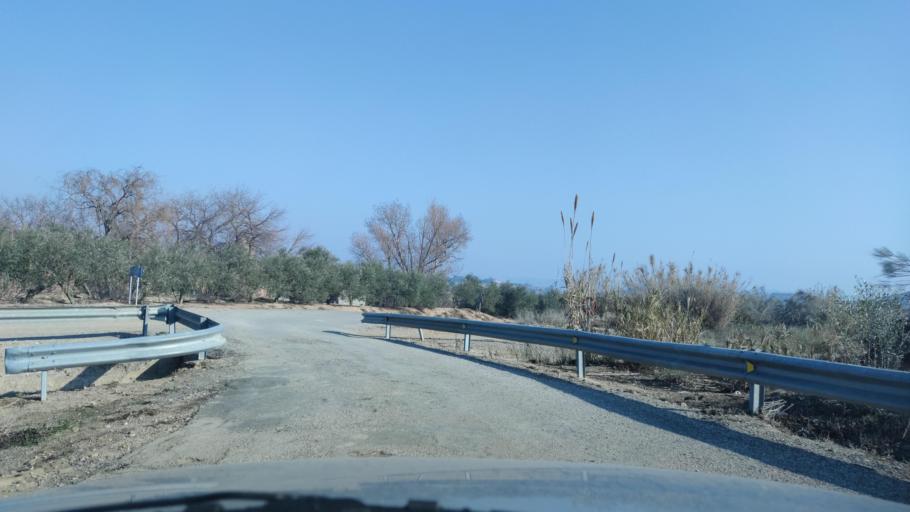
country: ES
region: Catalonia
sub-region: Provincia de Lleida
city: Seros
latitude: 41.4656
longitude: 0.3915
